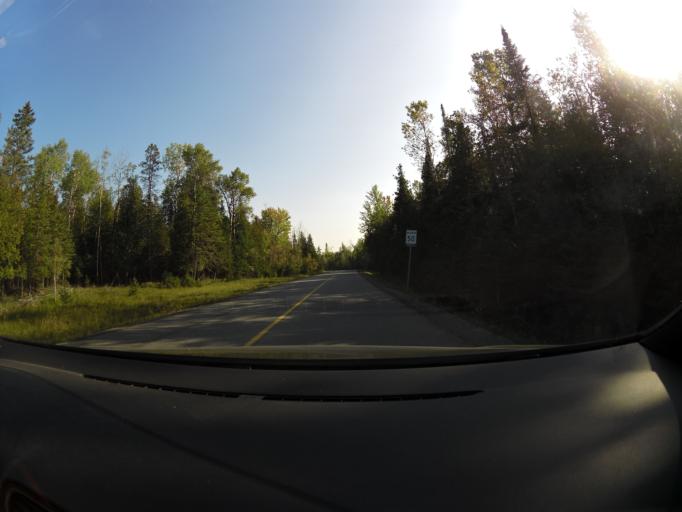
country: CA
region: Ontario
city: Arnprior
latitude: 45.4464
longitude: -76.2780
